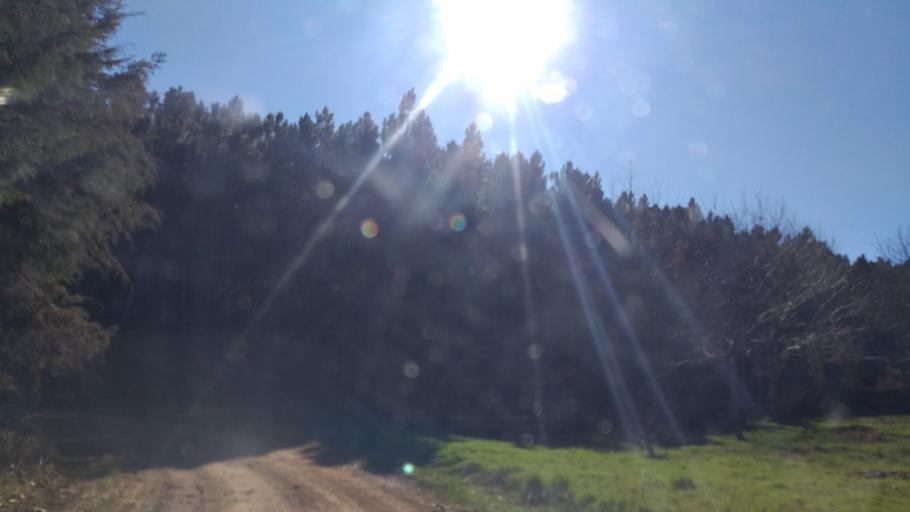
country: PT
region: Guarda
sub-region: Celorico da Beira
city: Celorico da Beira
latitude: 40.5185
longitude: -7.4132
